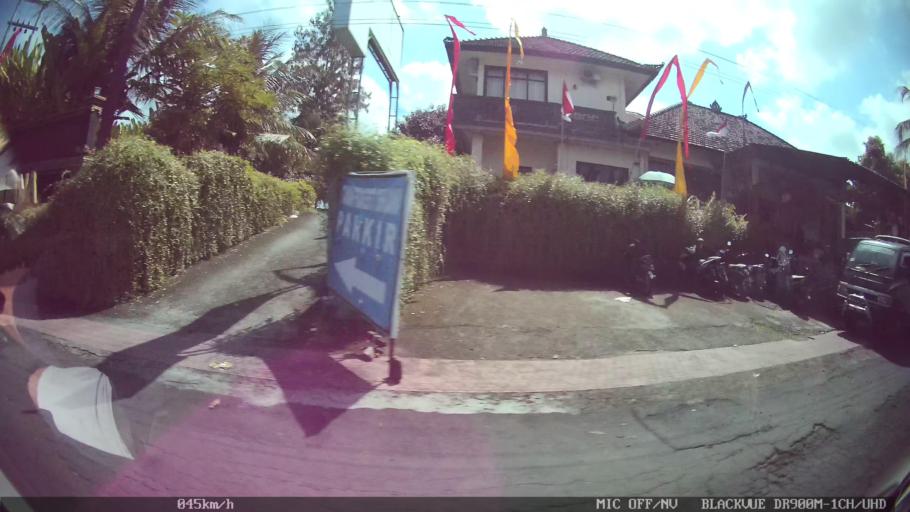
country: ID
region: Bali
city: Banjar Kelodan
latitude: -8.5251
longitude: 115.3287
